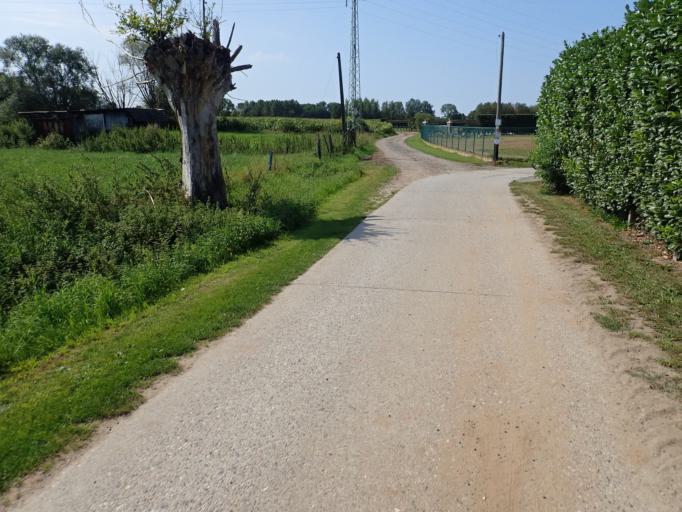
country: BE
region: Flanders
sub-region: Provincie Oost-Vlaanderen
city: Buggenhout
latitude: 51.0241
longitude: 4.2122
